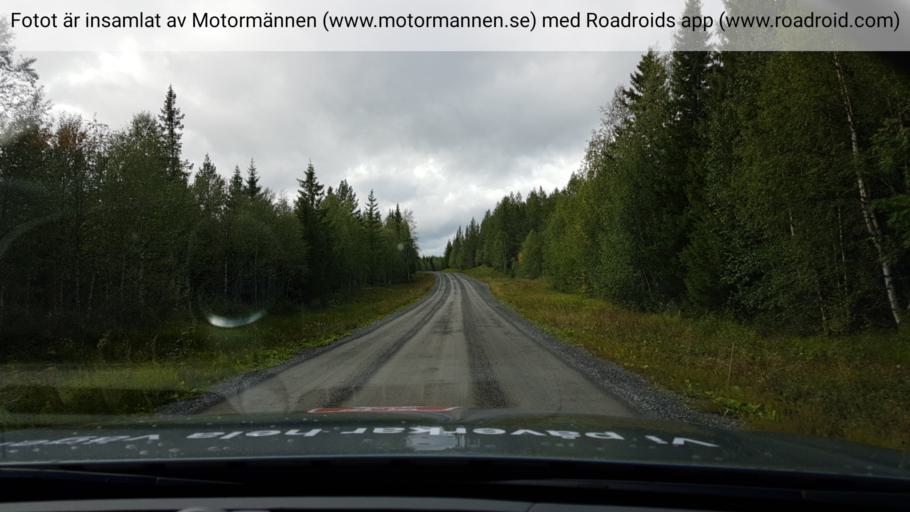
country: SE
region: Jaemtland
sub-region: Krokoms Kommun
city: Krokom
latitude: 63.7388
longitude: 14.4820
